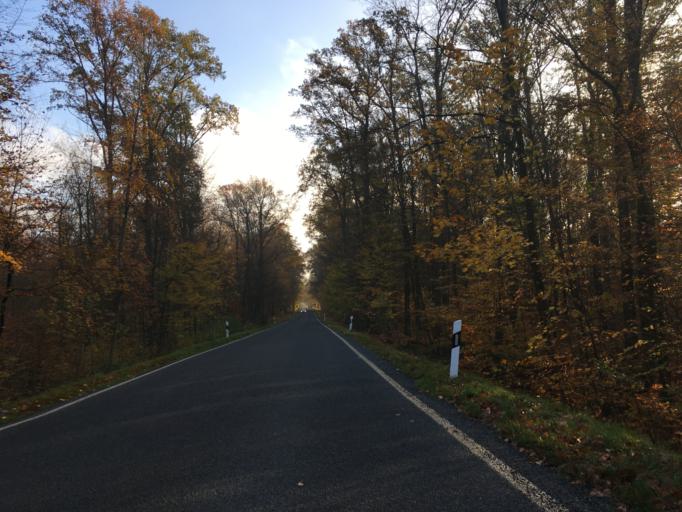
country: DE
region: Brandenburg
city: Schlepzig
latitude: 52.0299
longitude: 13.8698
